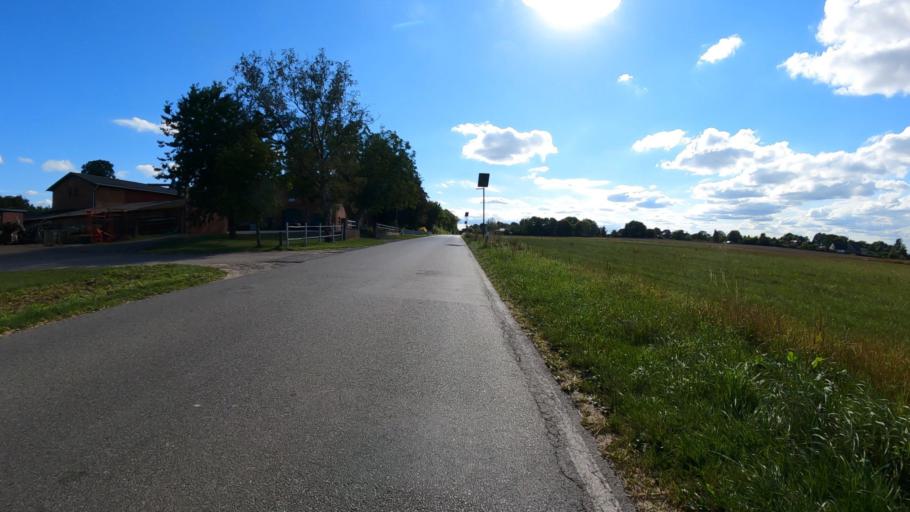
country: DE
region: Schleswig-Holstein
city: Stubben
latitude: 53.7223
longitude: 10.4127
